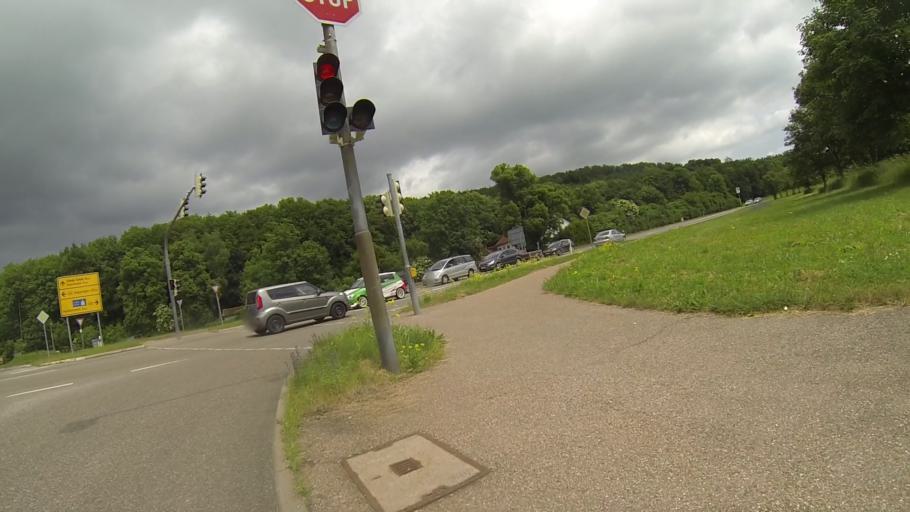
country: DE
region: Baden-Wuerttemberg
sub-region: Regierungsbezirk Stuttgart
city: Steinheim am Albuch
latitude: 48.6798
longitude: 10.1044
